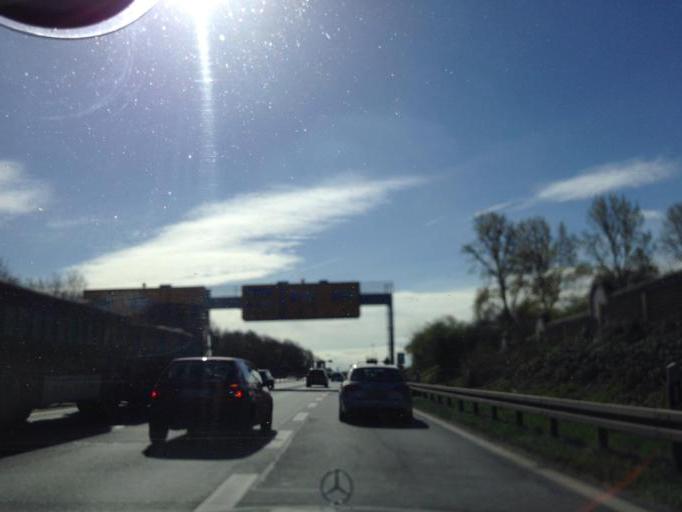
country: DE
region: Lower Saxony
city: Laatzen
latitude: 52.3348
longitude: 9.8089
